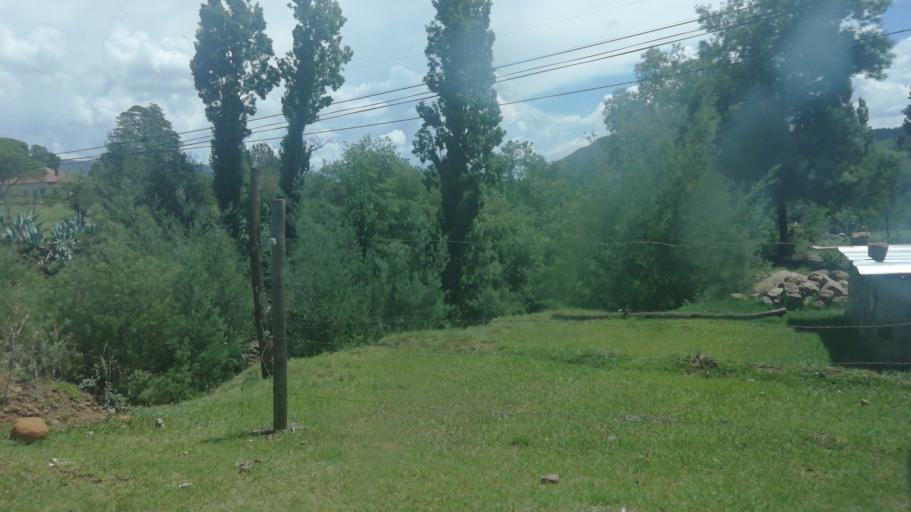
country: LS
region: Maseru
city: Nako
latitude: -29.6216
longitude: 27.5166
